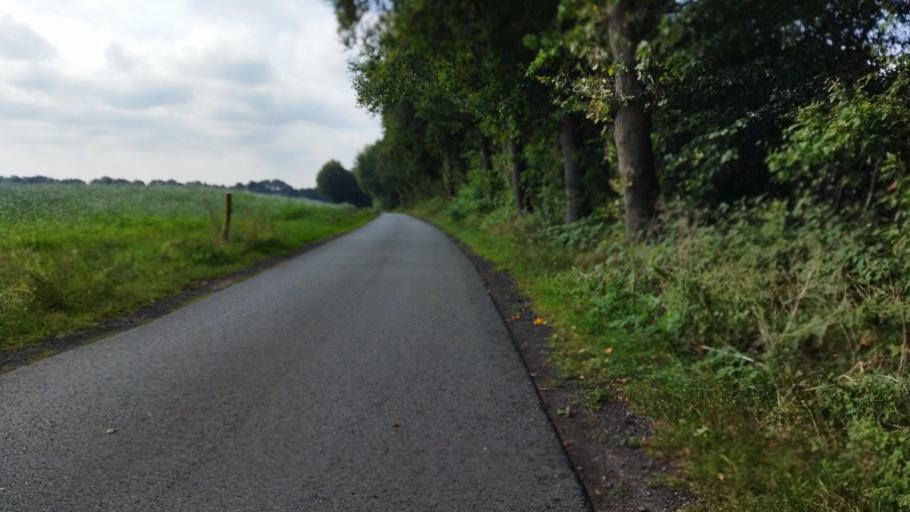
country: DE
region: North Rhine-Westphalia
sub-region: Regierungsbezirk Munster
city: Sassenberg
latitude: 52.0205
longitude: 8.0615
